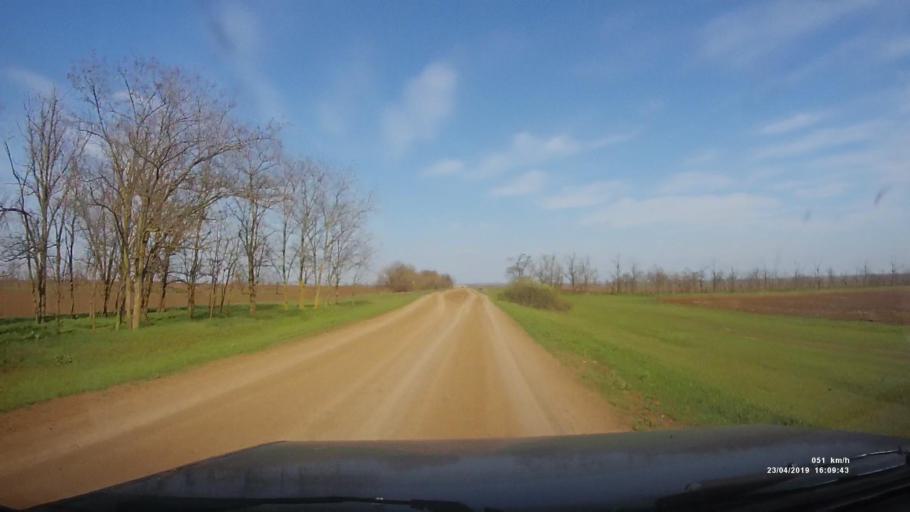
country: RU
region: Rostov
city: Remontnoye
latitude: 46.4816
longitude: 43.1141
